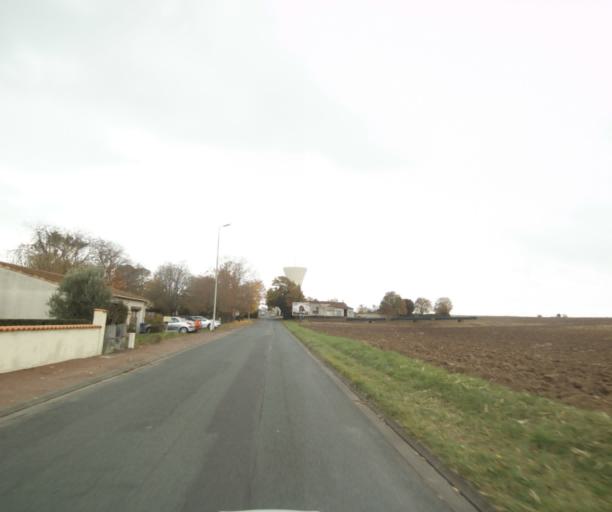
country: FR
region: Poitou-Charentes
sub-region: Departement de la Charente-Maritime
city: Saintes
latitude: 45.7345
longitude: -0.6534
